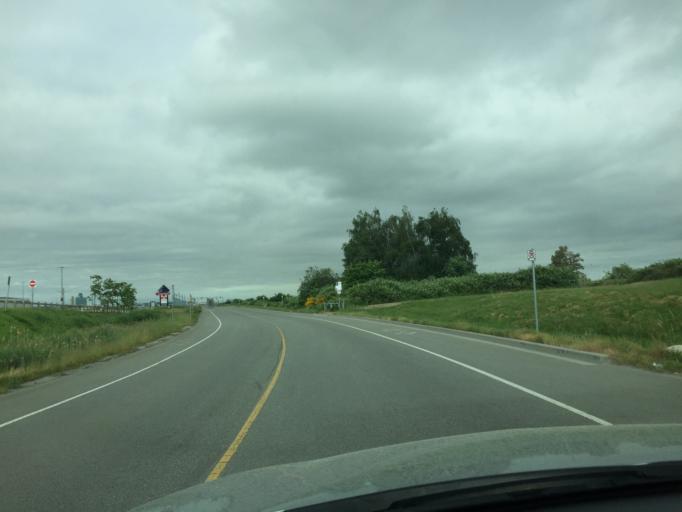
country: CA
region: British Columbia
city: Richmond
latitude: 49.1993
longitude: -123.1420
